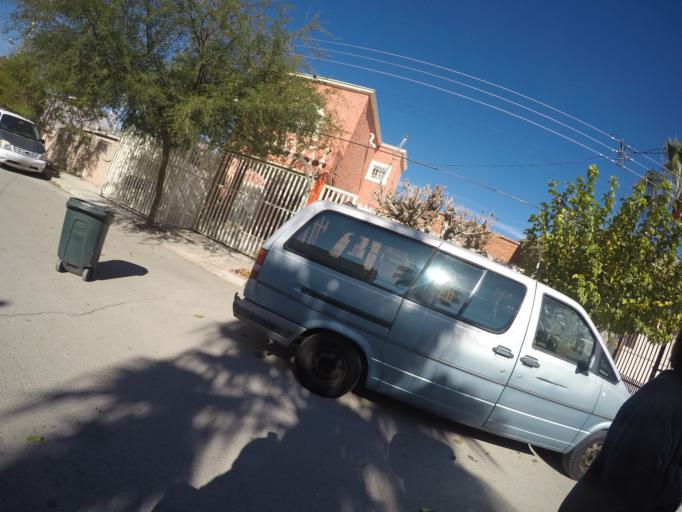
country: MX
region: Chihuahua
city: Ciudad Juarez
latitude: 31.7294
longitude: -106.4299
